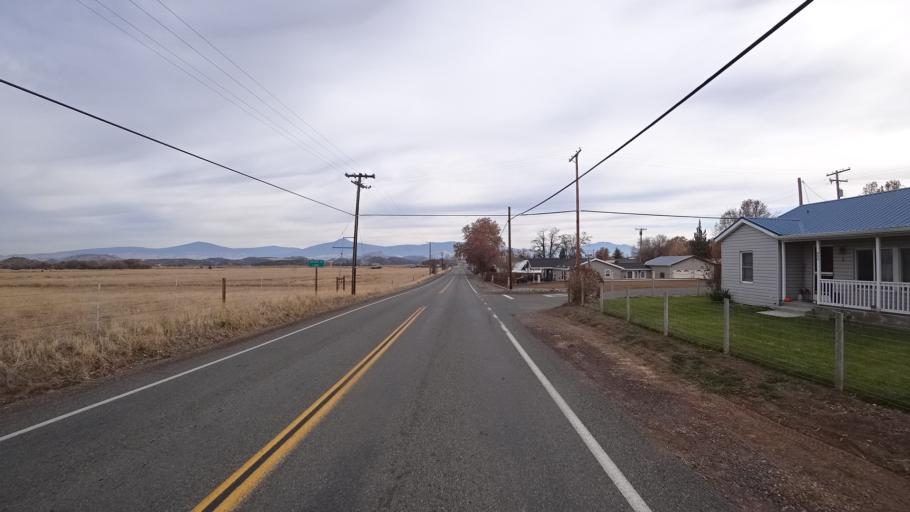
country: US
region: California
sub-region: Siskiyou County
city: Montague
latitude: 41.6472
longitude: -122.5254
